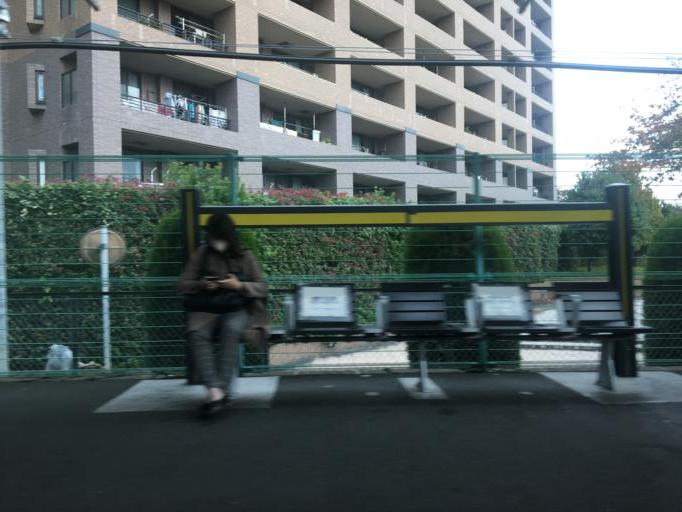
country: JP
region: Tokyo
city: Hino
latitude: 35.6939
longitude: 139.4240
